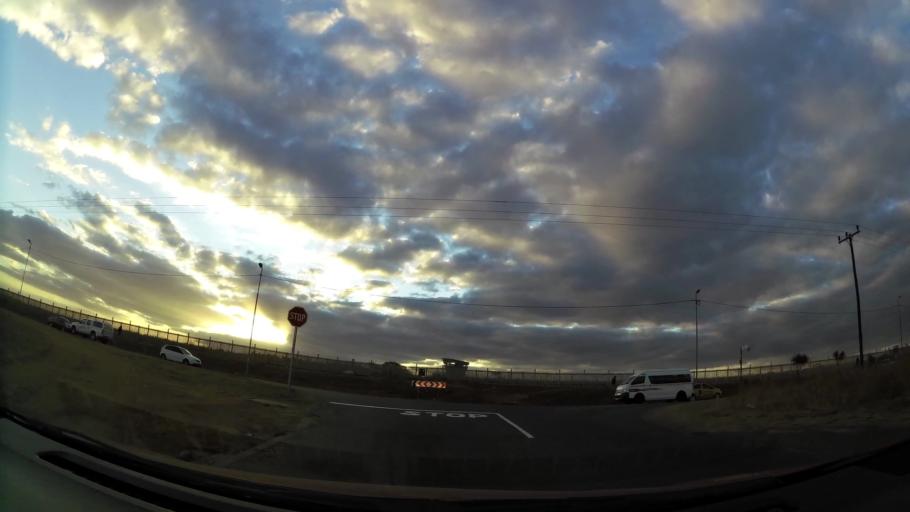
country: ZA
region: Gauteng
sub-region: City of Johannesburg Metropolitan Municipality
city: Midrand
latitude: -25.9976
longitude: 28.1424
